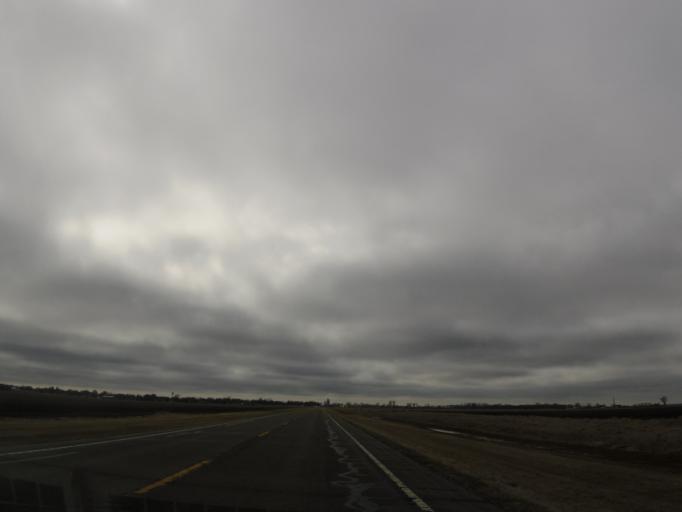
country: US
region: North Dakota
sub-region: Cass County
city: Casselton
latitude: 46.9182
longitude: -97.2204
